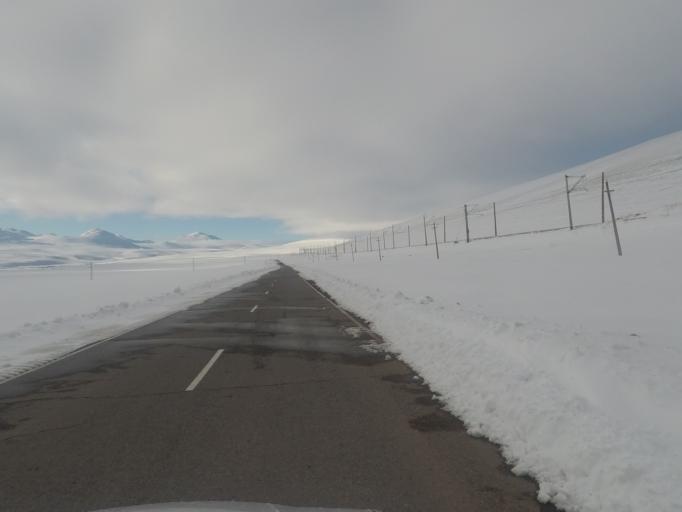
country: GE
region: Kvemo Kartli
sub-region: Tsalka
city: Tsalka
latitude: 41.4646
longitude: 43.8601
